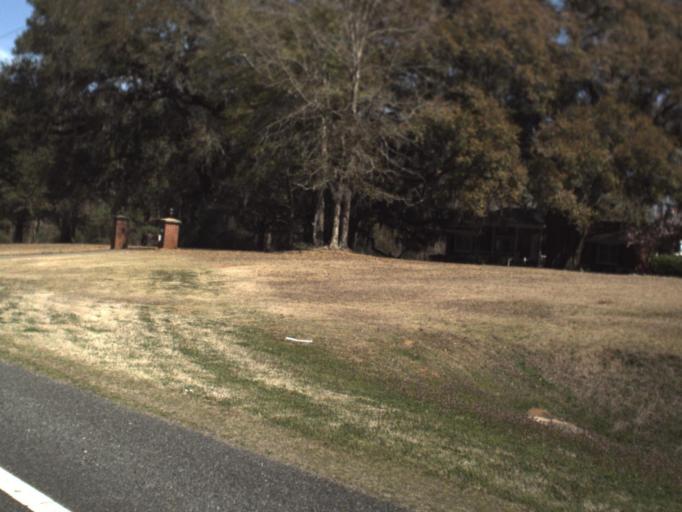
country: US
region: Florida
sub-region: Jackson County
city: Graceville
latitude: 30.9831
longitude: -85.4072
